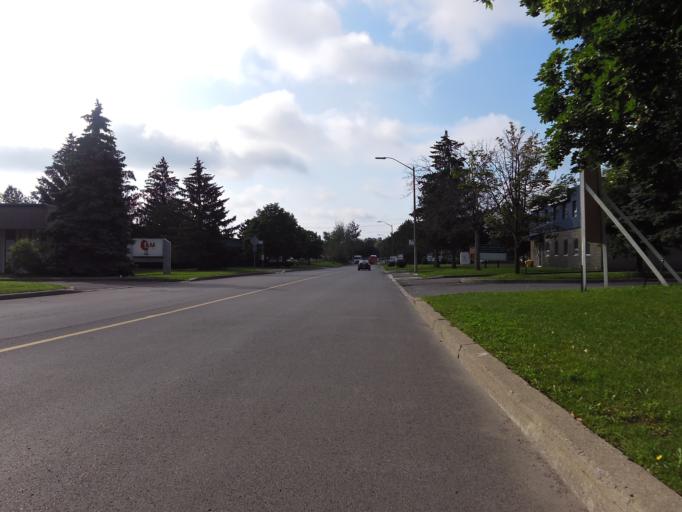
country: CA
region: Ontario
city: Ottawa
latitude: 45.3313
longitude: -75.7097
